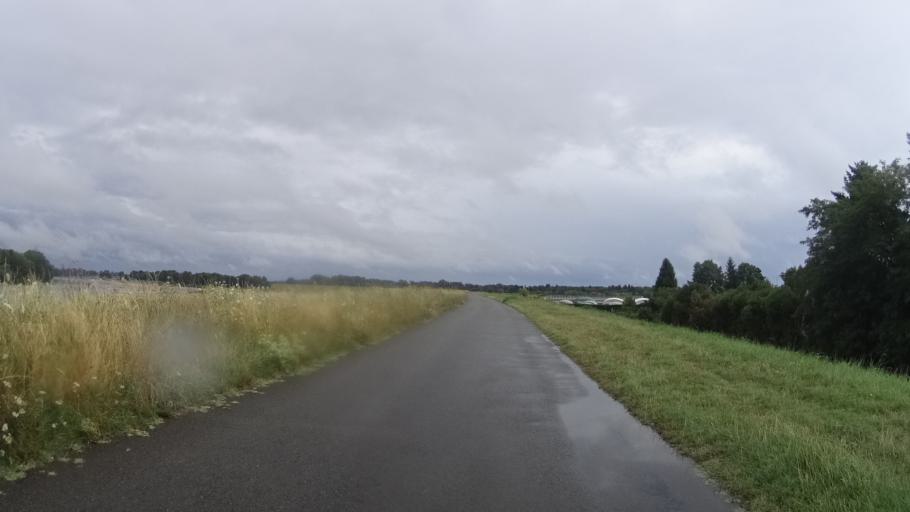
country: FR
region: Centre
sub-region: Departement du Loiret
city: Checy
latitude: 47.8897
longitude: 1.9951
